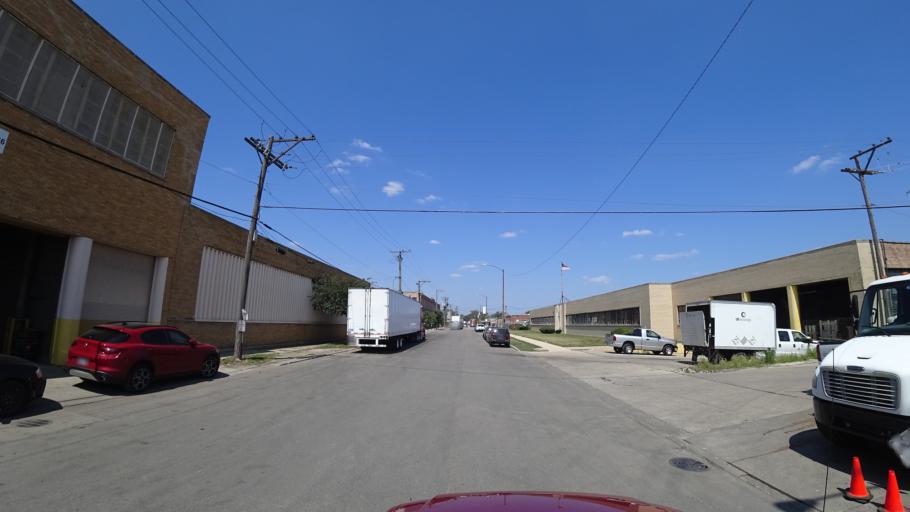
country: US
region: Illinois
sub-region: Cook County
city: Cicero
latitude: 41.8540
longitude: -87.7370
